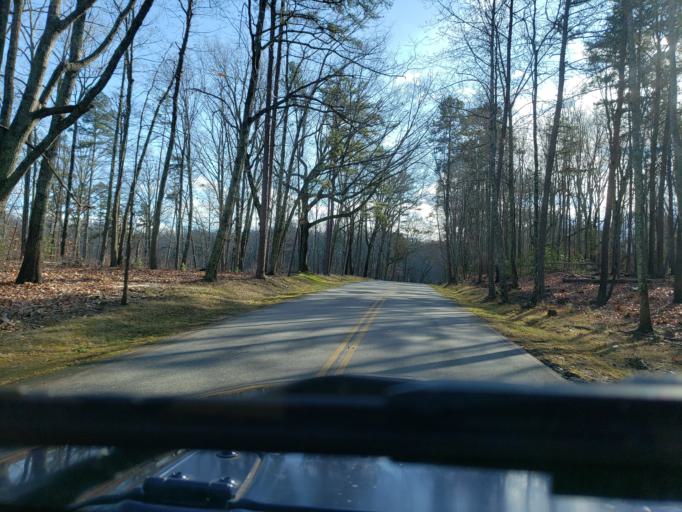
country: US
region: North Carolina
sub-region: Cleveland County
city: White Plains
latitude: 35.1435
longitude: -81.3873
